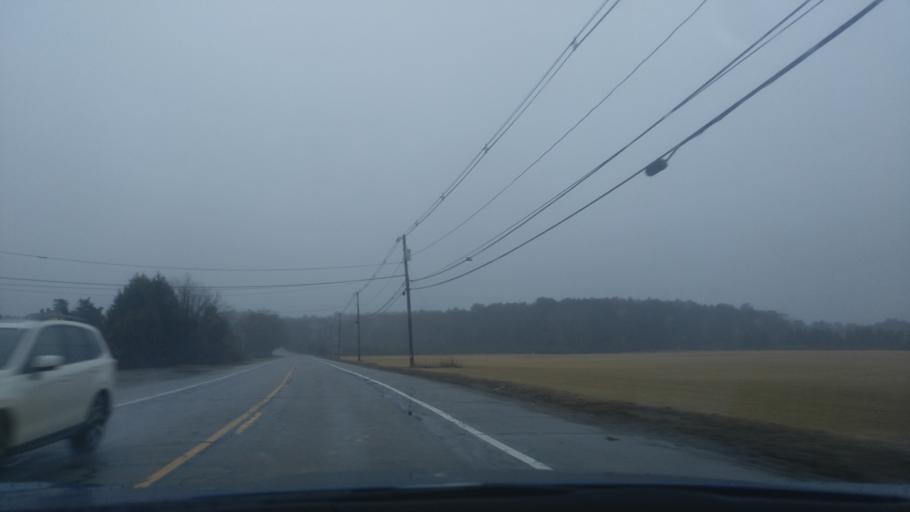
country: US
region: Rhode Island
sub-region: Washington County
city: Kingston
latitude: 41.4739
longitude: -71.6143
